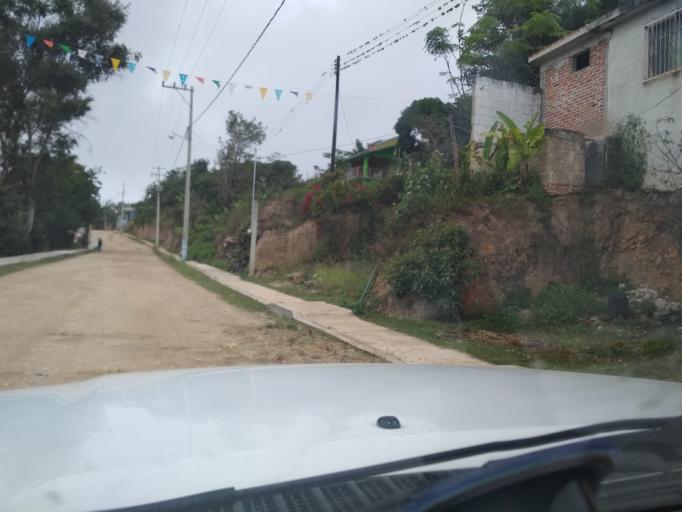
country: MX
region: Veracruz
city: El Castillo
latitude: 19.5448
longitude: -96.8286
